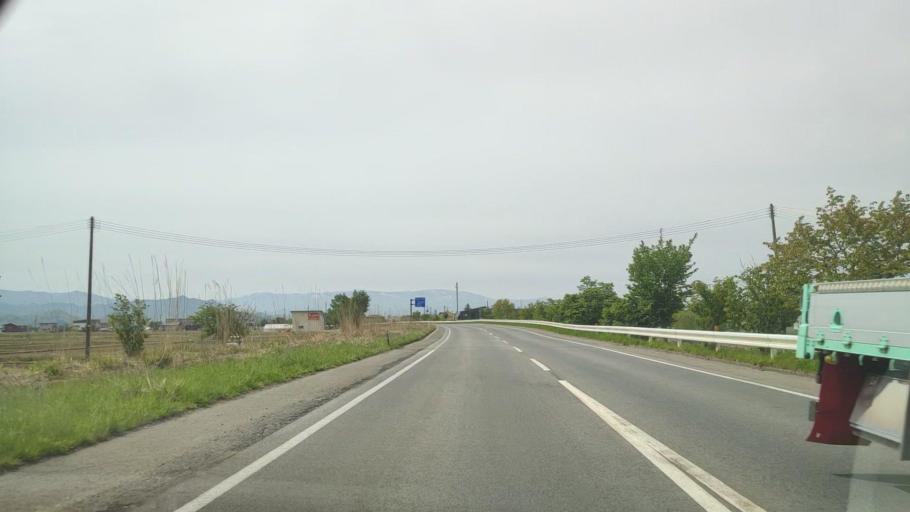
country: JP
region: Yamagata
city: Takahata
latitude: 38.0539
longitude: 140.1736
